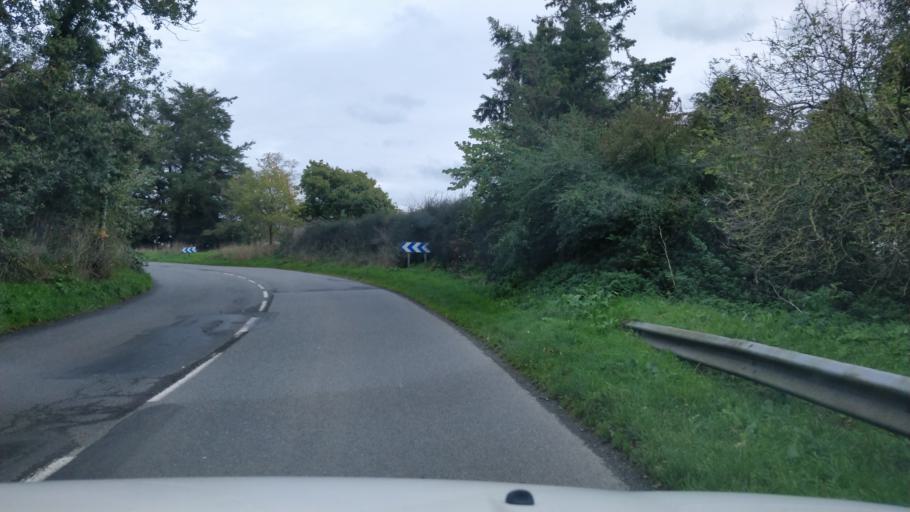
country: FR
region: Brittany
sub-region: Departement des Cotes-d'Armor
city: La Roche-Derrien
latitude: 48.7491
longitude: -3.2689
